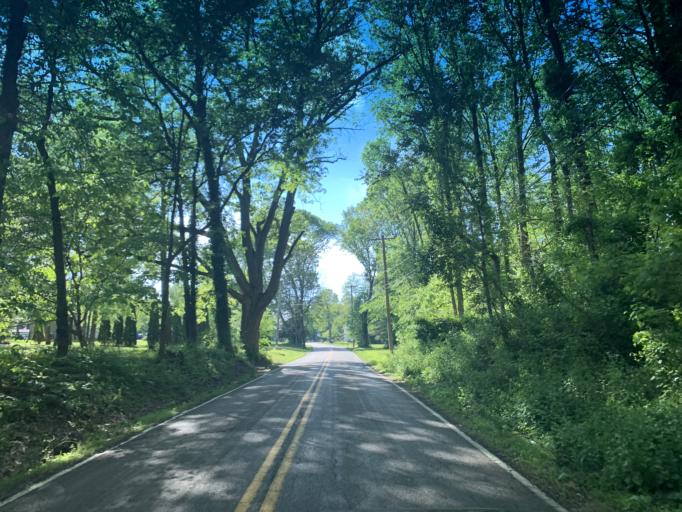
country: US
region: Maryland
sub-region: Cecil County
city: Rising Sun
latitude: 39.6969
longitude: -76.1590
